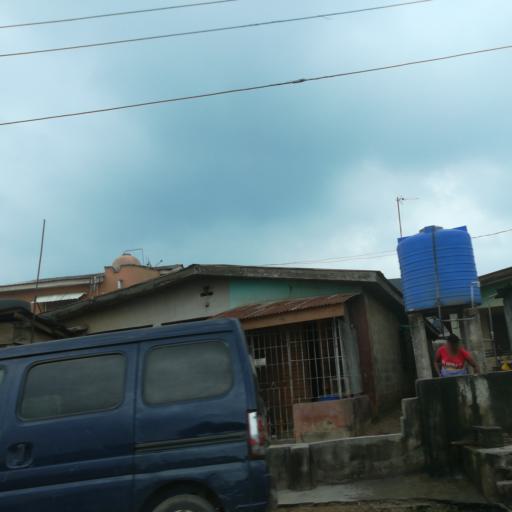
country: NG
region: Lagos
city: Agege
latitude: 6.5940
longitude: 3.2999
